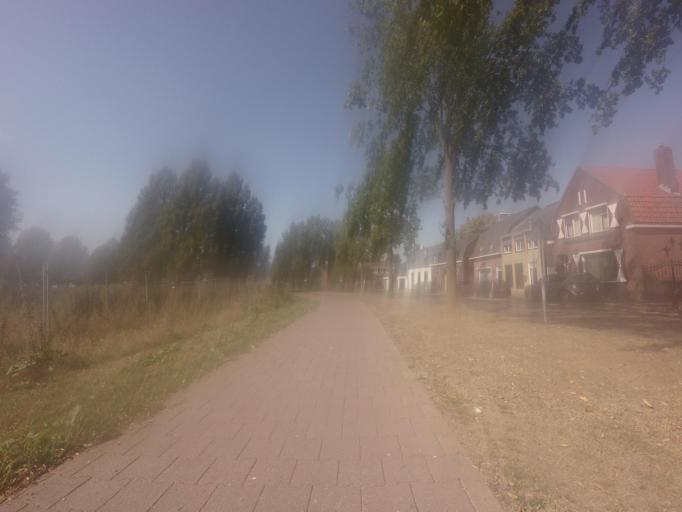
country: NL
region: North Brabant
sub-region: Gemeente Goirle
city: Goirle
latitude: 51.5201
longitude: 5.0755
